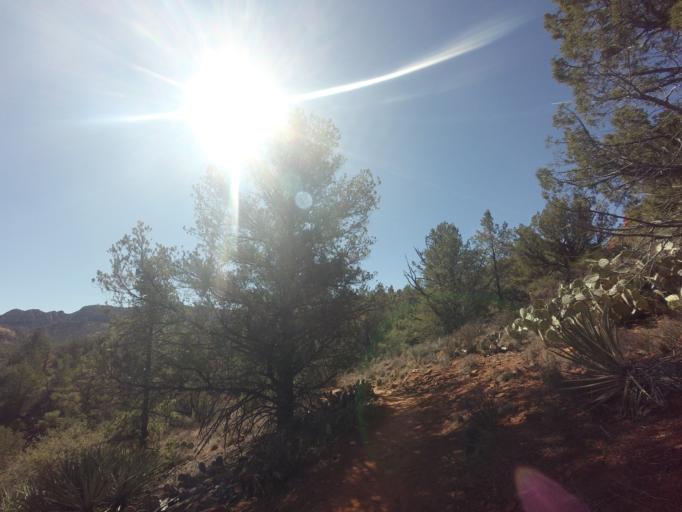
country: US
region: Arizona
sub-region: Yavapai County
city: West Sedona
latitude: 34.8072
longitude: -111.8267
